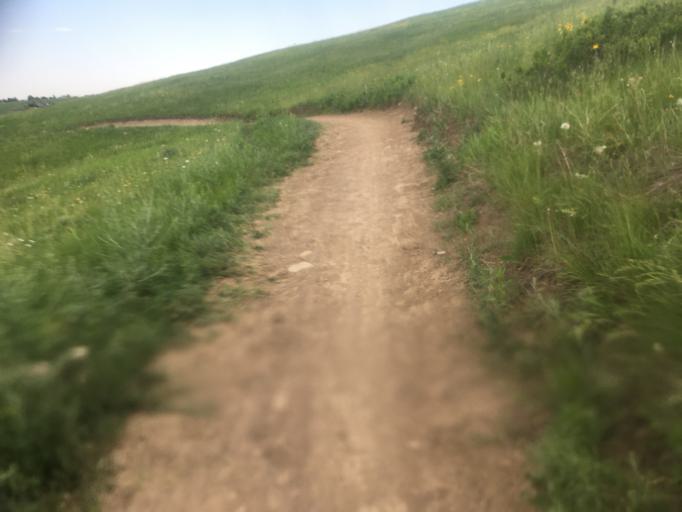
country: US
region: Colorado
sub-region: Boulder County
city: Superior
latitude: 39.9581
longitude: -105.2065
